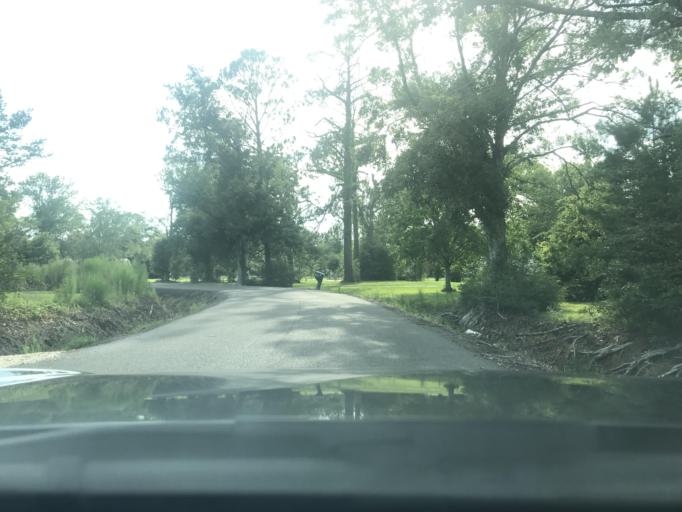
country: US
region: Louisiana
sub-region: Calcasieu Parish
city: Moss Bluff
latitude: 30.3400
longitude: -93.2583
